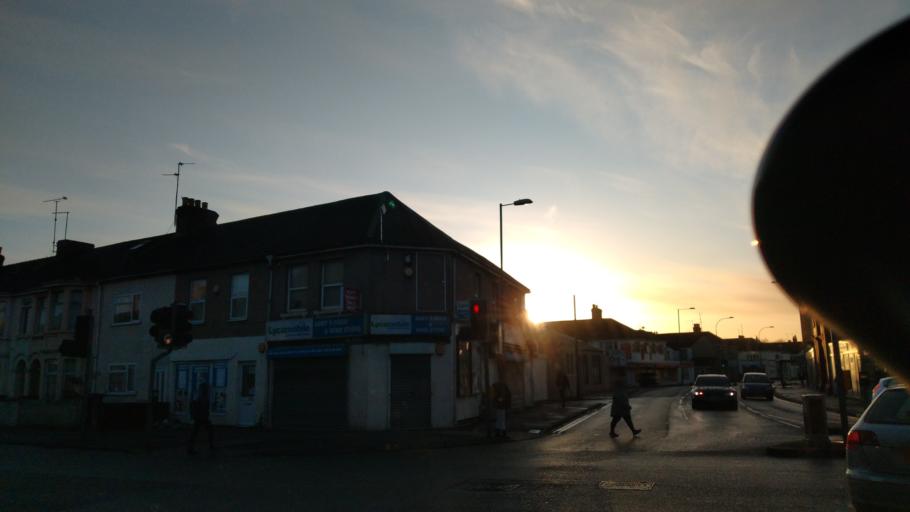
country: GB
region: England
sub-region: Borough of Swindon
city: Swindon
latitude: 51.5650
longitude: -1.7813
